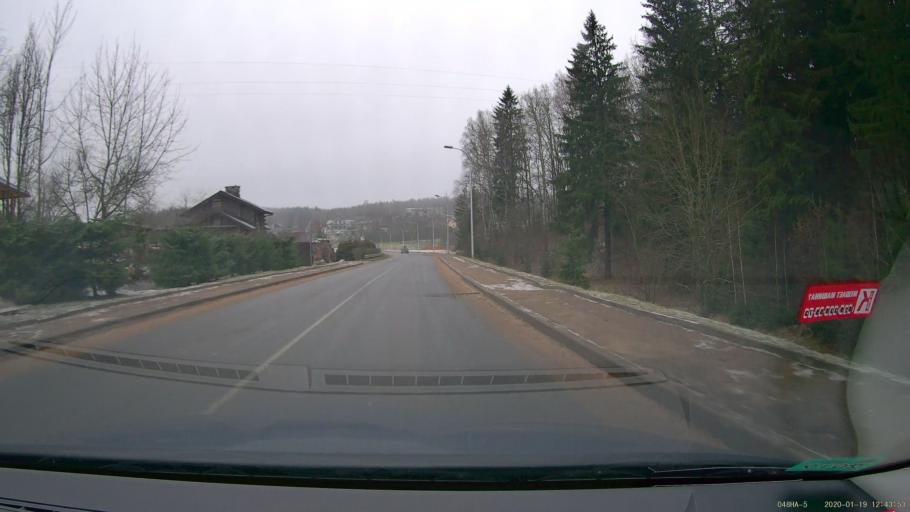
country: BY
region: Minsk
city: Lahoysk
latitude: 54.1780
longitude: 27.8098
